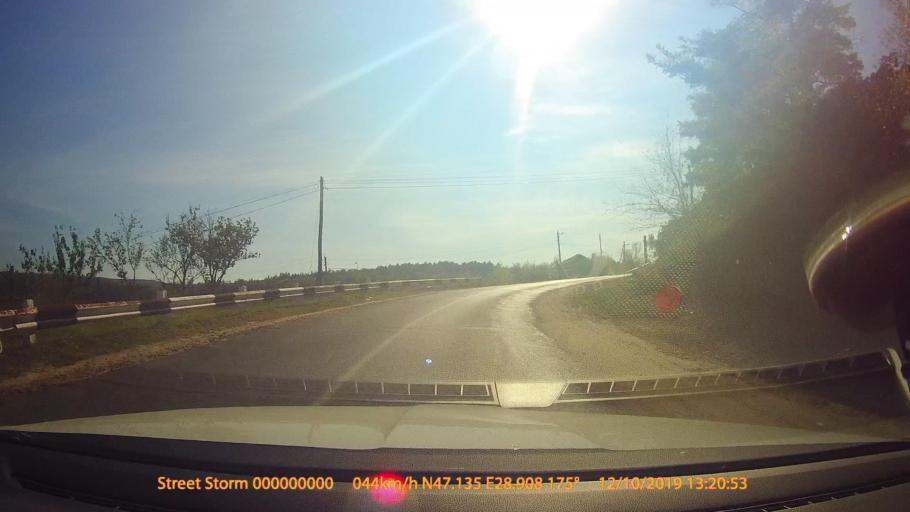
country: MD
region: Chisinau
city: Ciorescu
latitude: 47.1351
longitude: 28.9078
